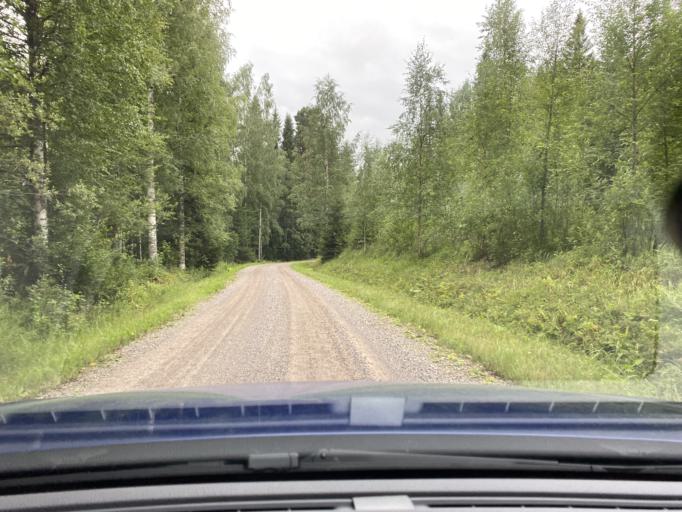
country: FI
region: Pirkanmaa
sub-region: Ylae-Pirkanmaa
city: Maenttae
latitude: 62.0188
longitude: 24.7524
